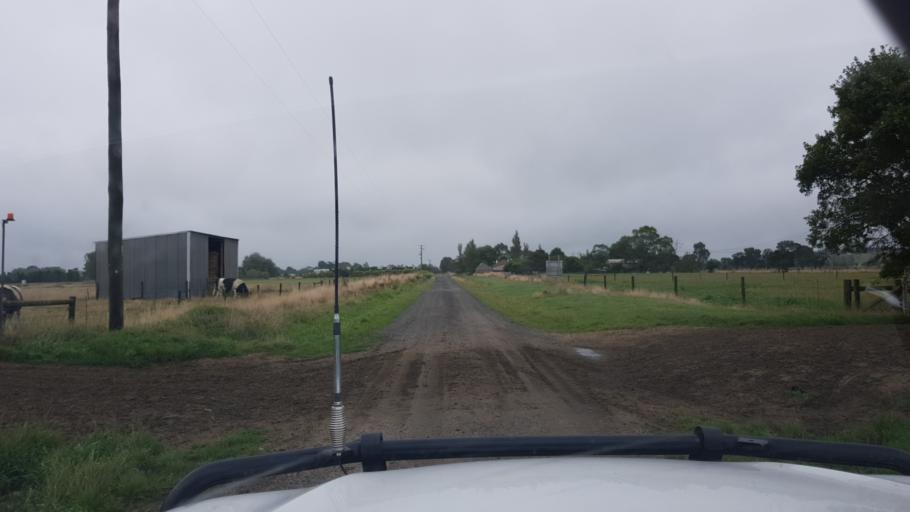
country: AU
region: Victoria
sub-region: Latrobe
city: Moe
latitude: -38.1905
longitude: 146.1052
